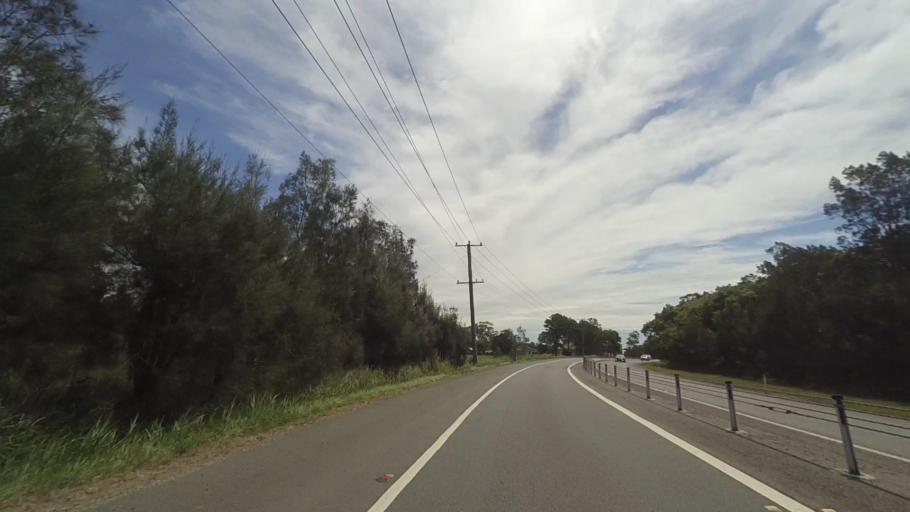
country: AU
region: New South Wales
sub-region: Port Stephens Shire
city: Medowie
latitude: -32.7902
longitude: 151.9183
